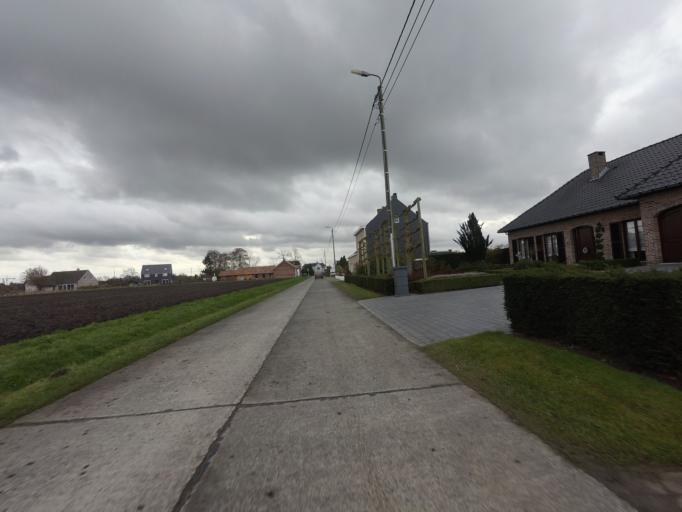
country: BE
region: Flanders
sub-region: Provincie Antwerpen
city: Sint-Katelijne-Waver
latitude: 51.0764
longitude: 4.5209
